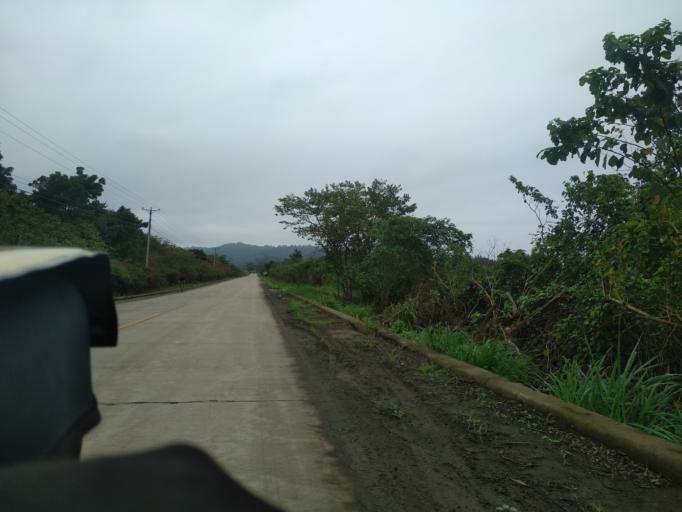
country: EC
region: Manabi
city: Jipijapa
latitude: -1.6583
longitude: -80.8183
